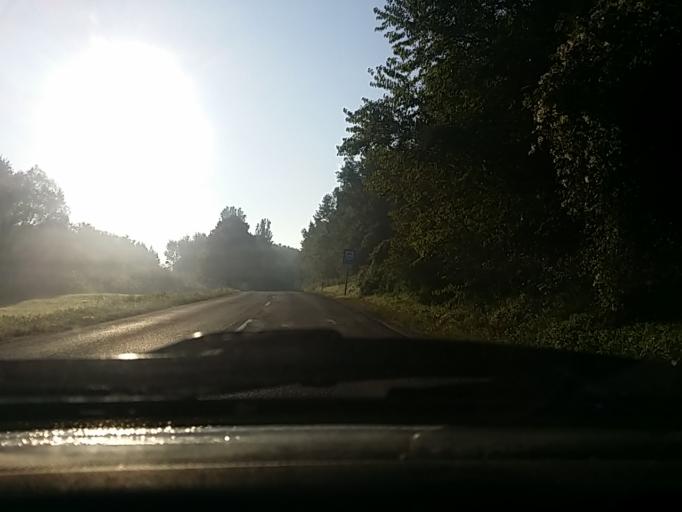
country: HU
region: Pest
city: Szob
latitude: 47.8014
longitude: 18.8542
